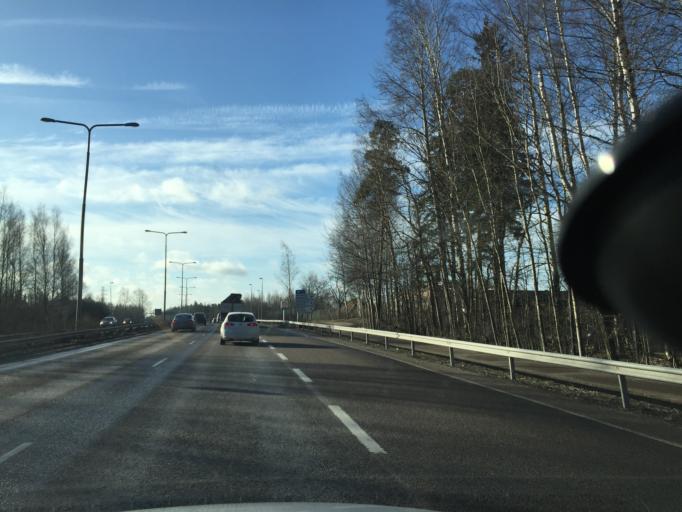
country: FI
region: Uusimaa
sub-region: Helsinki
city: Teekkarikylae
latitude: 60.2658
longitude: 24.8748
